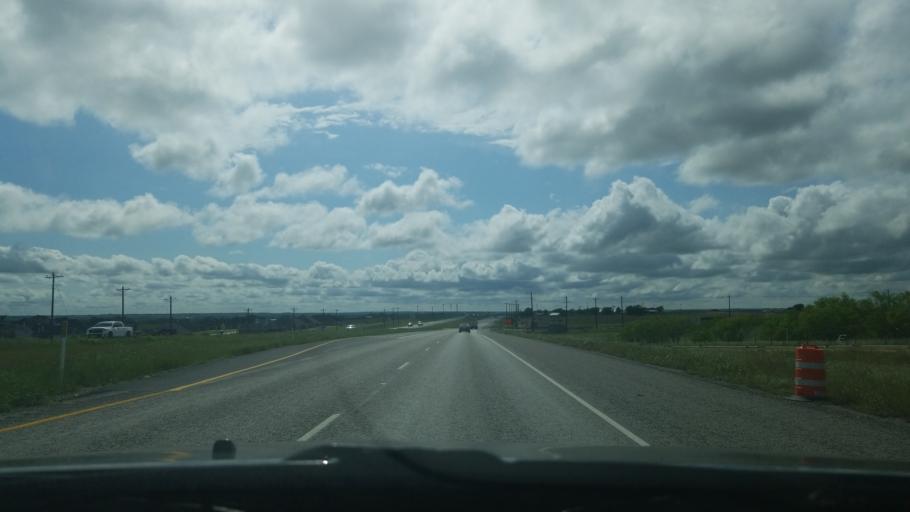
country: US
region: Texas
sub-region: Denton County
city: Ponder
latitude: 33.2415
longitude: -97.3593
